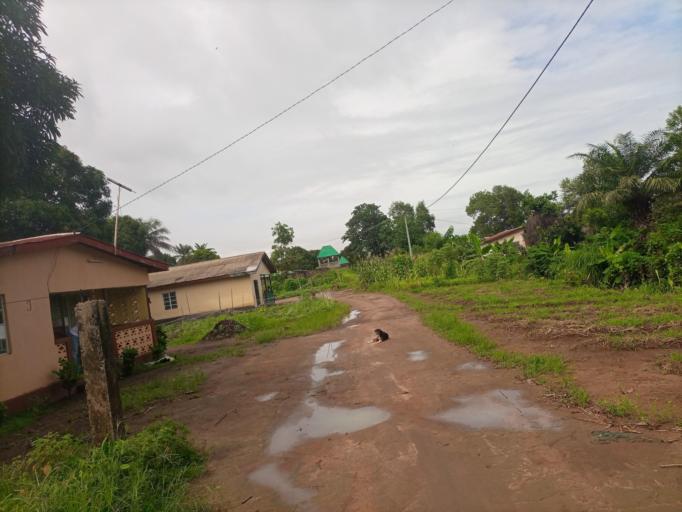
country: SL
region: Northern Province
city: Tintafor
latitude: 8.6233
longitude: -13.2077
